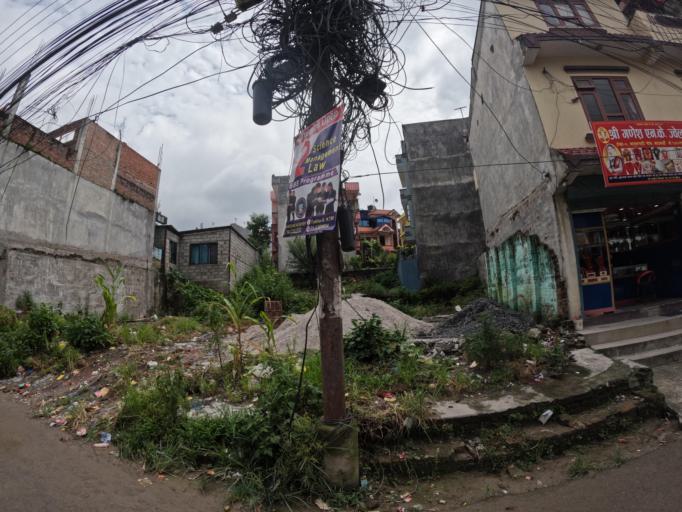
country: NP
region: Central Region
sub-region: Bagmati Zone
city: Kathmandu
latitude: 27.7504
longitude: 85.3180
